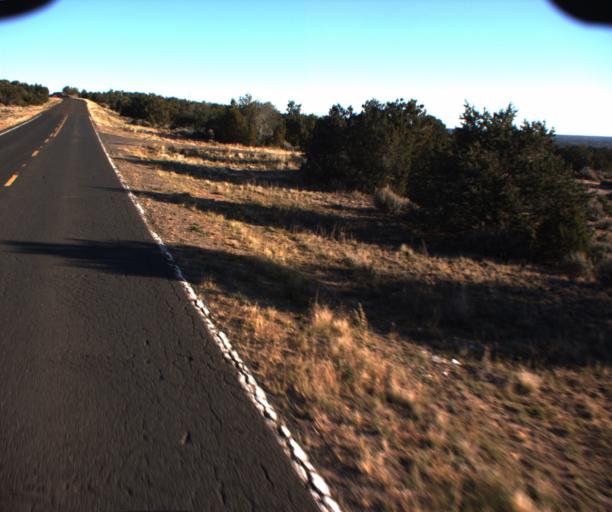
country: US
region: Arizona
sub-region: Apache County
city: Ganado
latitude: 35.5141
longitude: -109.5266
